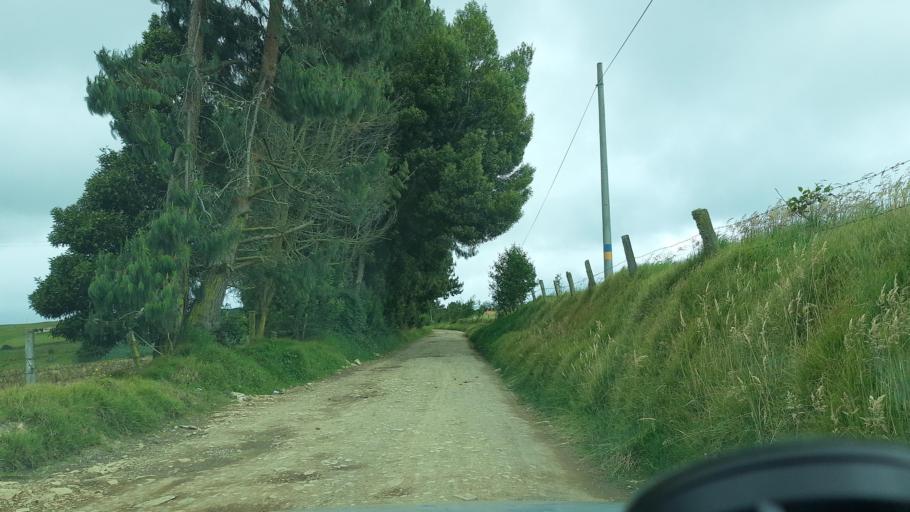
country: CO
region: Boyaca
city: Samaca
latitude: 5.4943
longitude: -73.4536
